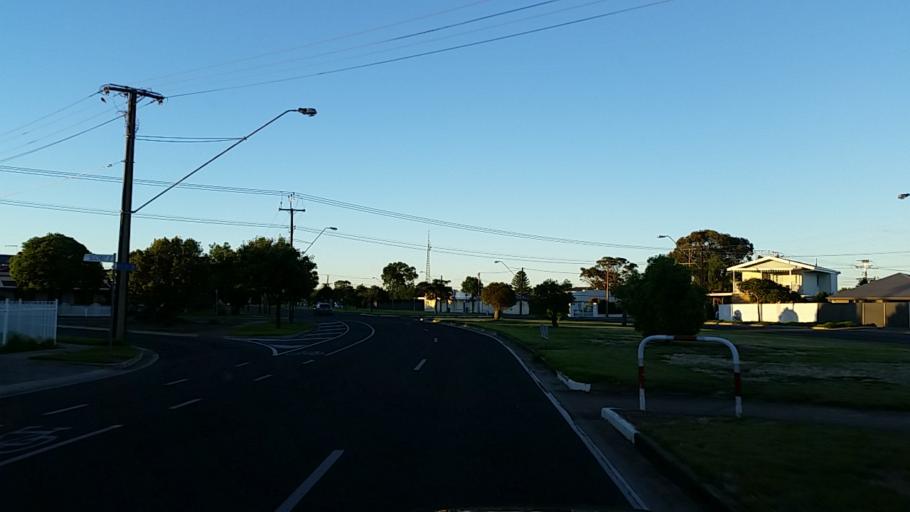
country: AU
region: South Australia
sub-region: City of West Torrens
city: Plympton
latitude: -34.9282
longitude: 138.5432
